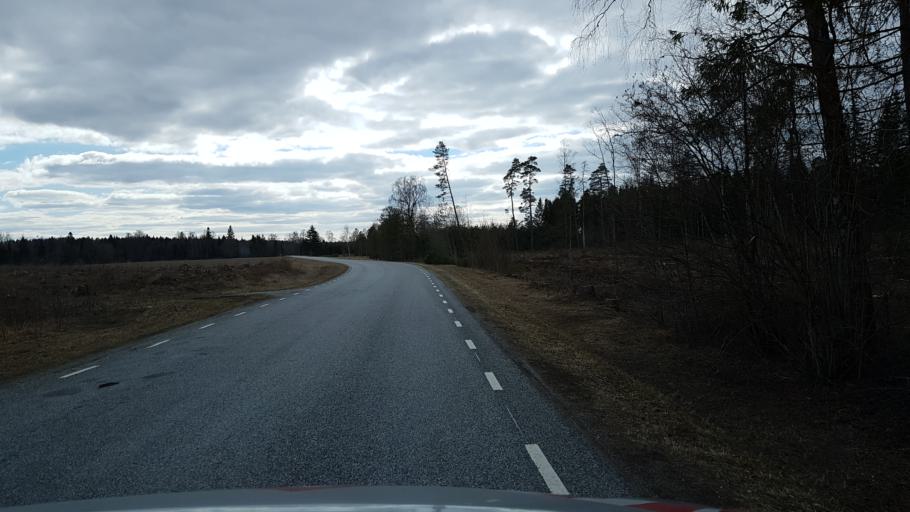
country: EE
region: Laeaene-Virumaa
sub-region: Tamsalu vald
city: Tamsalu
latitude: 59.2286
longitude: 26.1663
